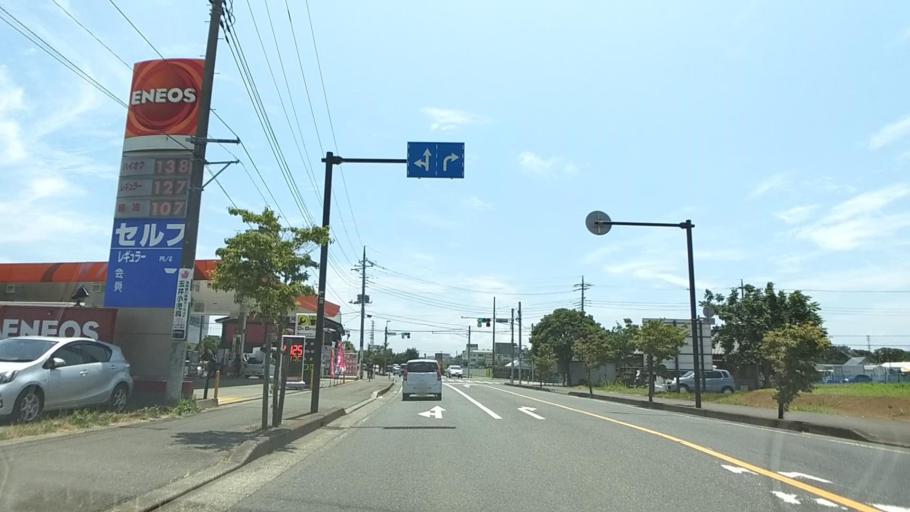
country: JP
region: Kanagawa
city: Chigasaki
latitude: 35.3773
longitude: 139.3848
